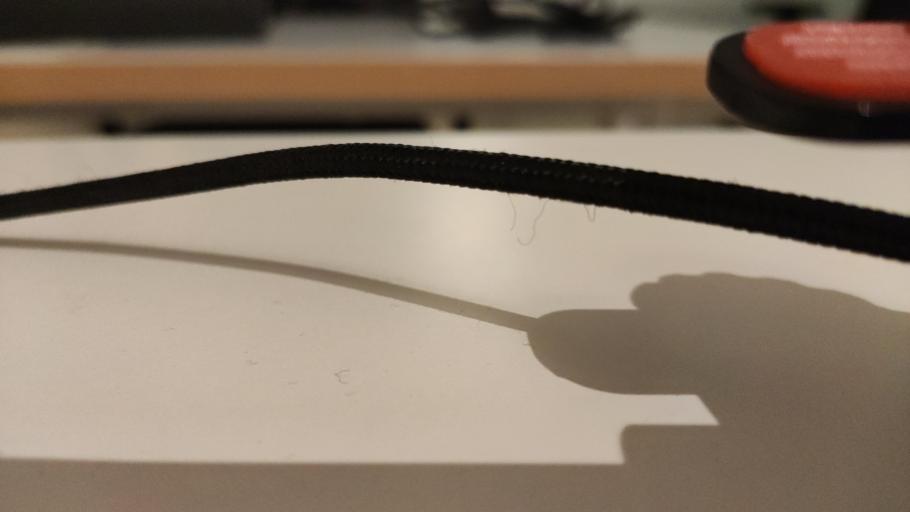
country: RU
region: Moskovskaya
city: Kurovskoye
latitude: 55.5788
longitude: 38.8887
